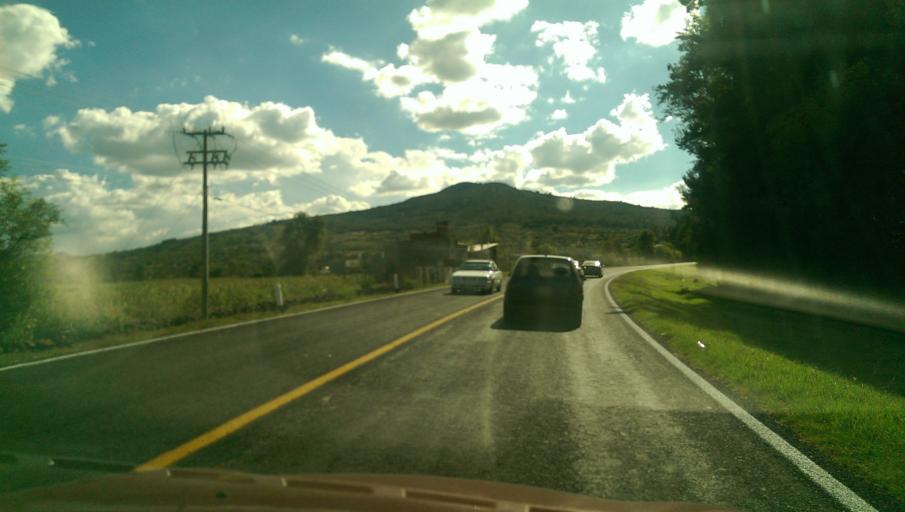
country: MX
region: Michoacan
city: Quiroga
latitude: 19.6426
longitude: -101.5358
